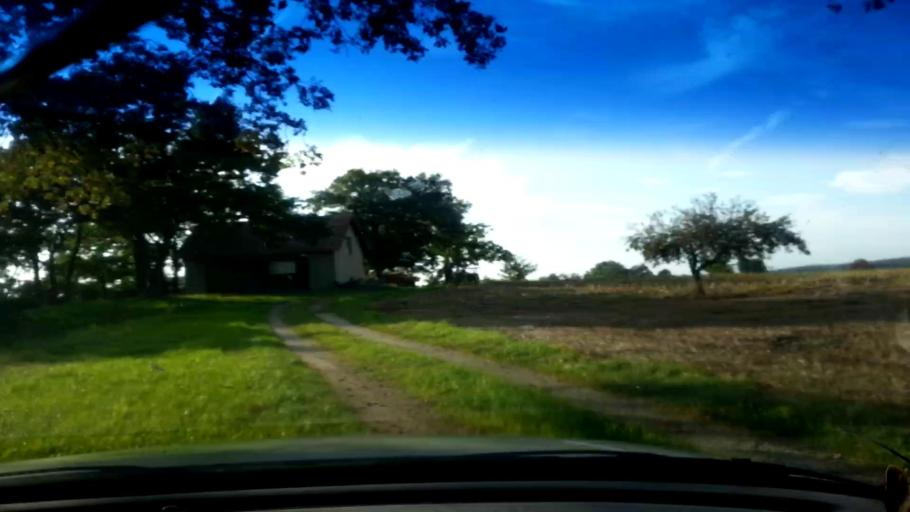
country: DE
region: Bavaria
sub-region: Upper Franconia
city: Viereth-Trunstadt
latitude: 49.9436
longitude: 10.7680
